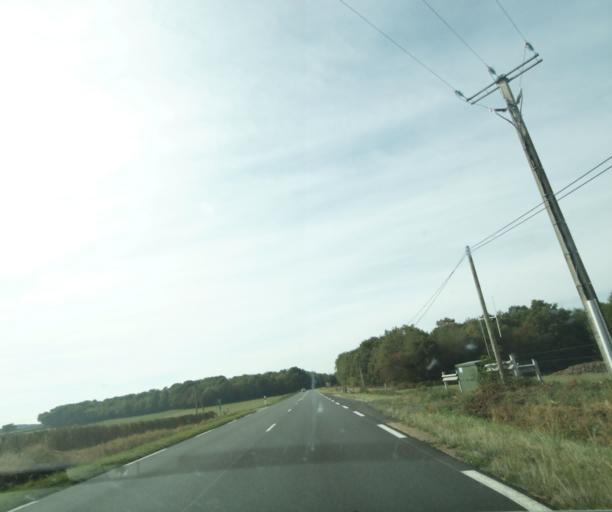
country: FR
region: Auvergne
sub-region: Departement de l'Allier
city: Saint-Francois
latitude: 46.4435
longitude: 3.9132
